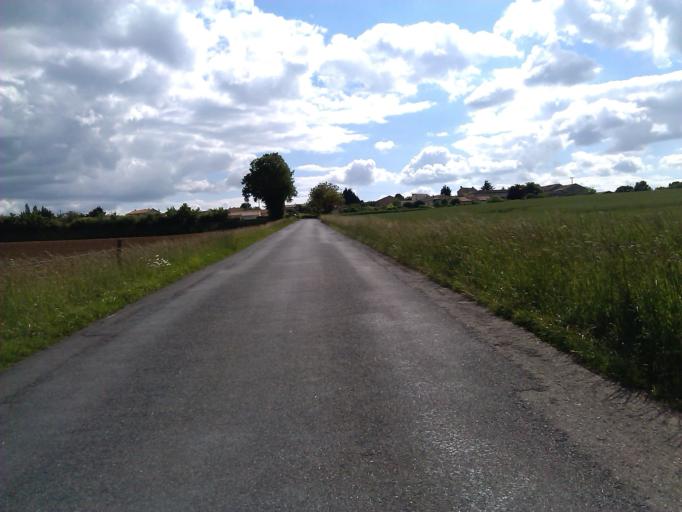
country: FR
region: Poitou-Charentes
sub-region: Departement de la Charente
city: Mansle
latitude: 45.8967
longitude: 0.2070
